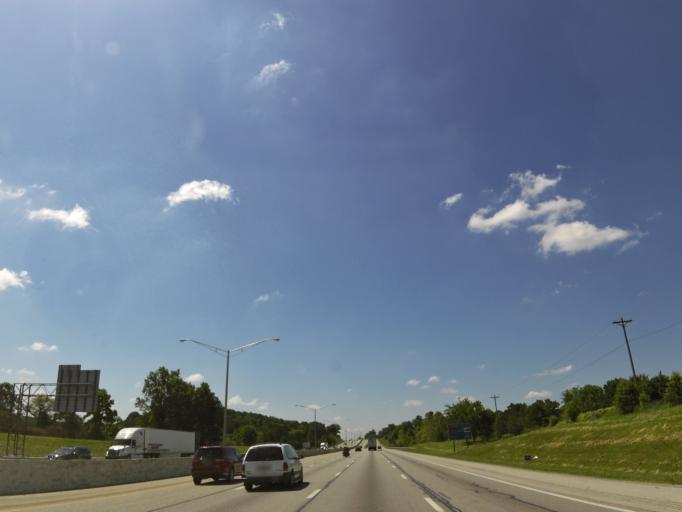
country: US
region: Kentucky
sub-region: Laurel County
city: London
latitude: 37.1281
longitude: -84.1077
